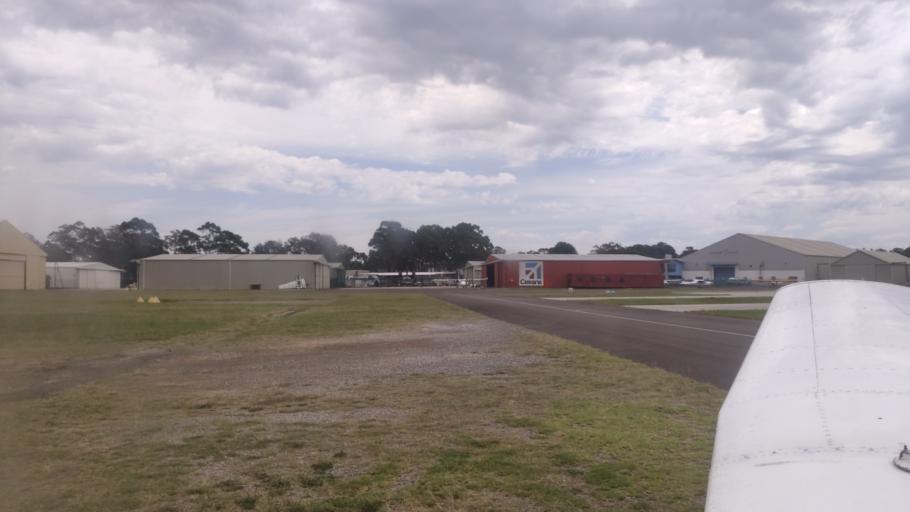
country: AU
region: New South Wales
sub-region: Bankstown
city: Milperra
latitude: -33.9207
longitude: 150.9939
